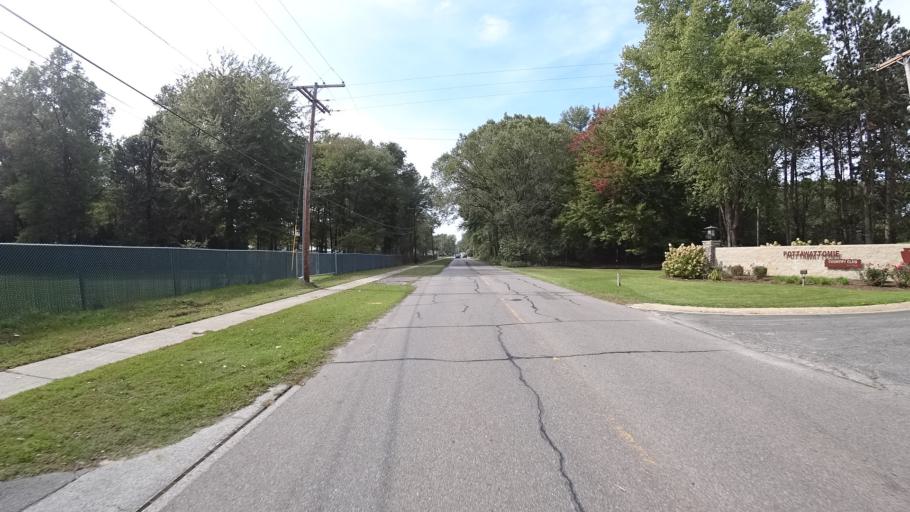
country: US
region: Indiana
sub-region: LaPorte County
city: Trail Creek
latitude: 41.7167
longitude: -86.8627
